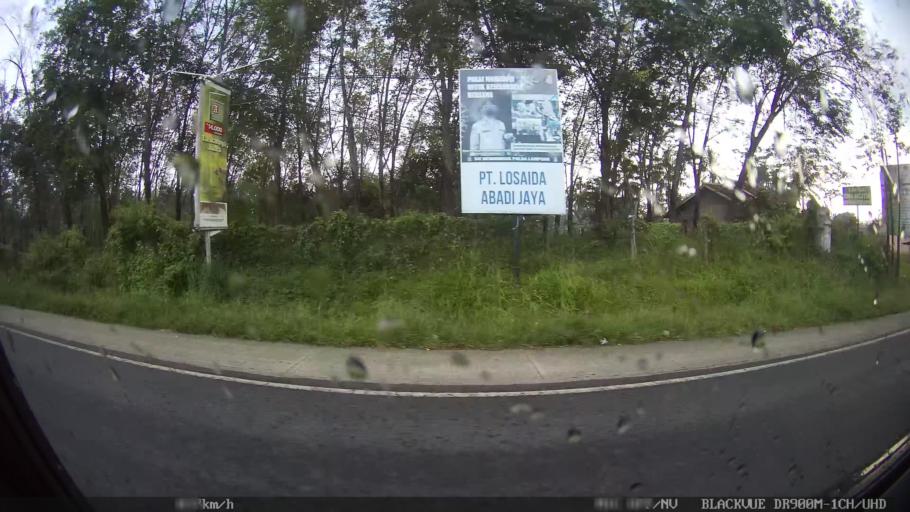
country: ID
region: Lampung
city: Gedongtataan
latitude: -5.3798
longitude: 105.1156
